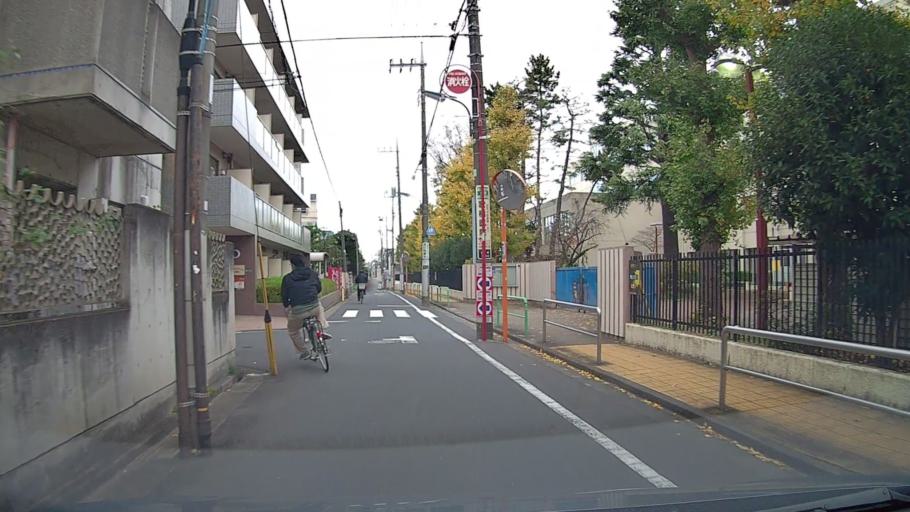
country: JP
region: Saitama
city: Wako
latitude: 35.7390
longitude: 139.6259
